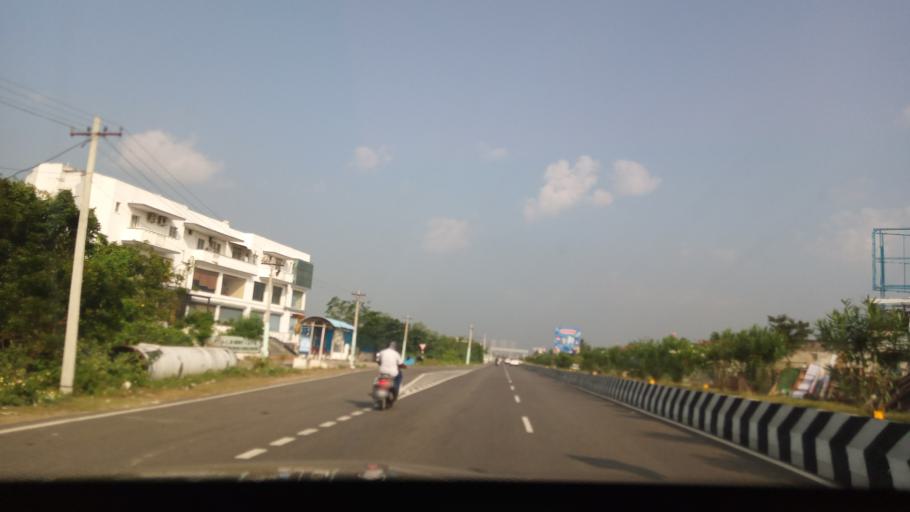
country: IN
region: Tamil Nadu
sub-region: Kancheepuram
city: Injambakkam
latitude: 12.7785
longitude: 80.2483
